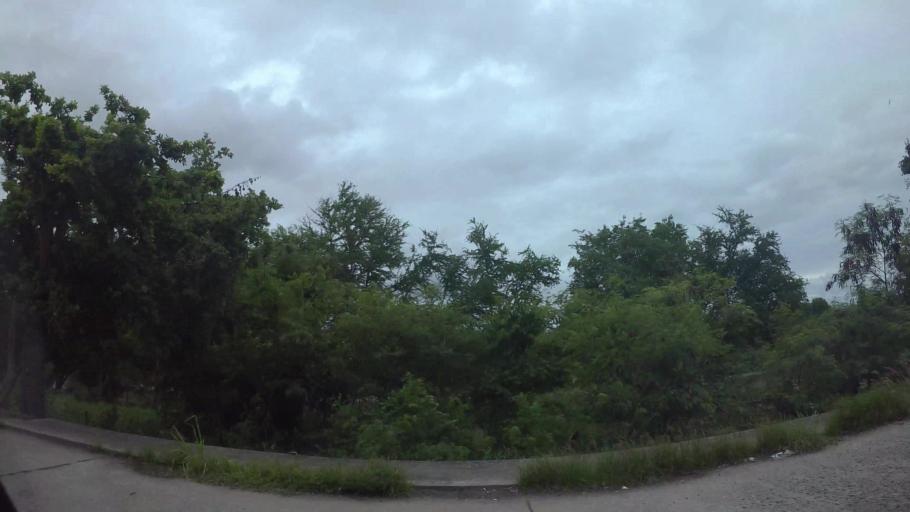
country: TH
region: Rayong
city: Rayong
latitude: 12.6658
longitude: 101.2796
